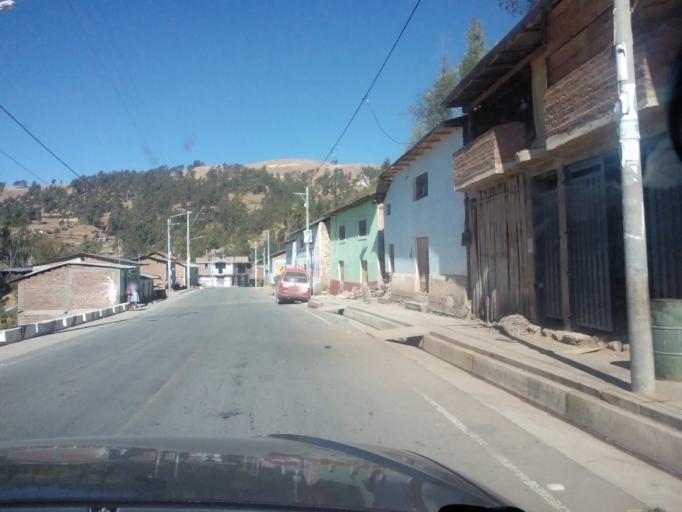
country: PE
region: Apurimac
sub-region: Provincia de Andahuaylas
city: Talavera
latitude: -13.6565
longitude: -73.4968
